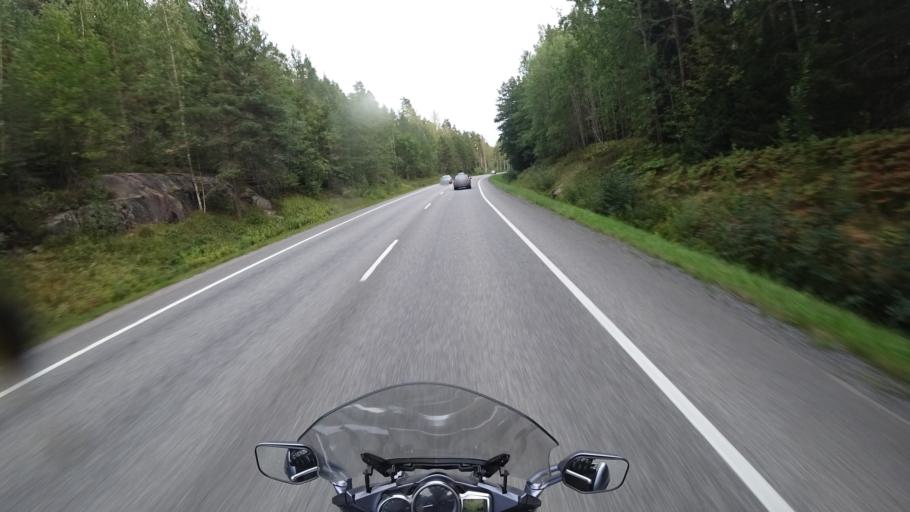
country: FI
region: Uusimaa
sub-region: Raaseporin
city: Karis
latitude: 60.0853
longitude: 23.6583
